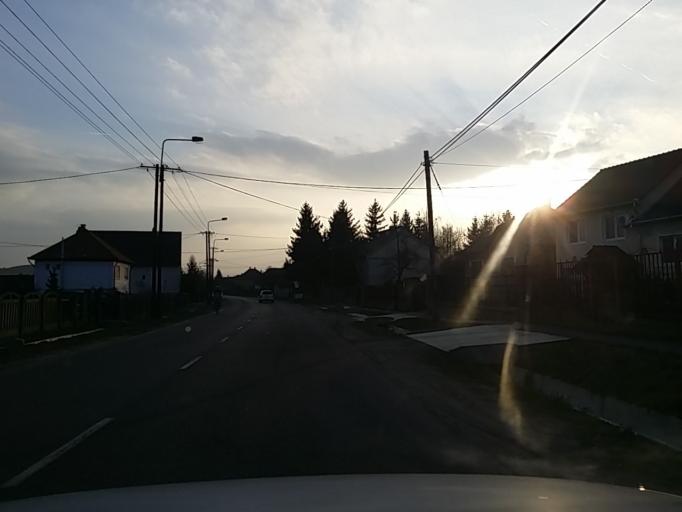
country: HU
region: Heves
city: Tarnalelesz
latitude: 48.0609
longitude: 20.1883
